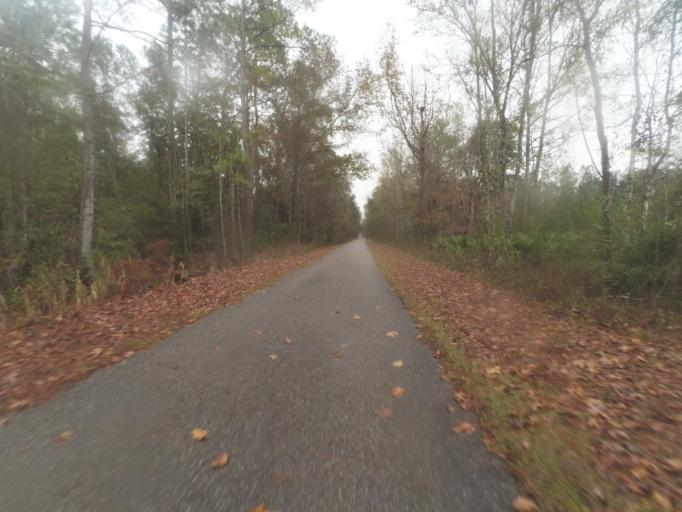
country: US
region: Florida
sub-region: Alachua County
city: Hawthorne
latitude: 29.5876
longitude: -82.1002
